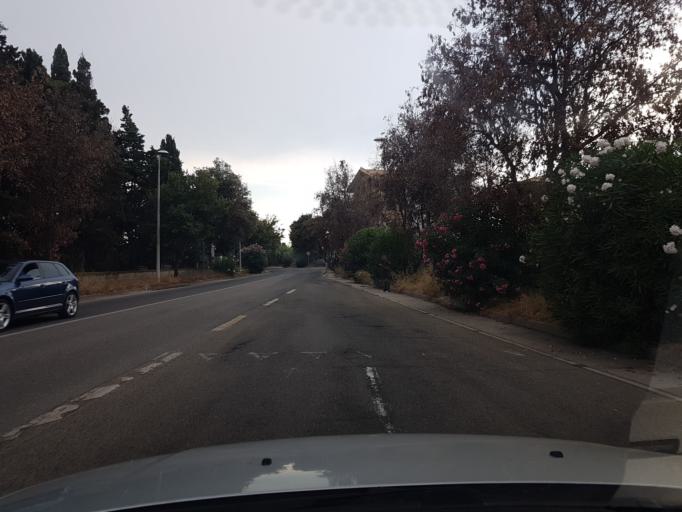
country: IT
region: Sardinia
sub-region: Provincia di Oristano
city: Donigala Fenugheddu
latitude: 39.9265
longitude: 8.5769
